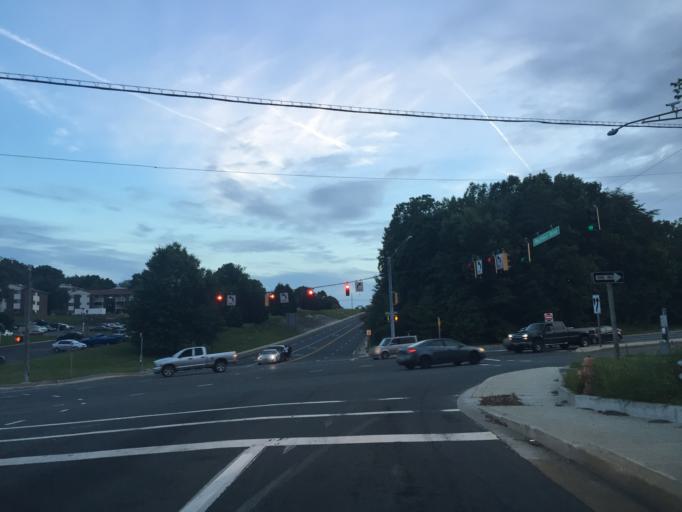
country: US
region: Maryland
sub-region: Baltimore County
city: Carney
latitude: 39.3814
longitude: -76.5122
